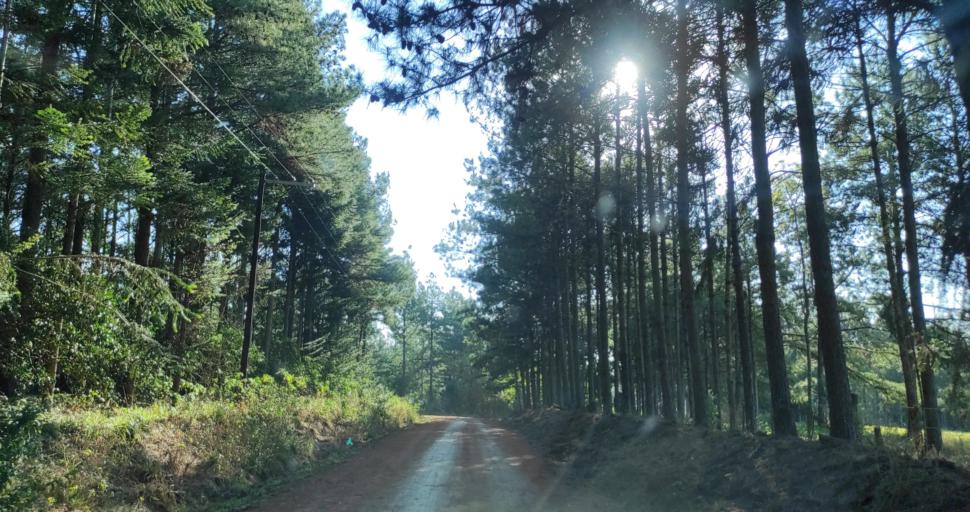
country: AR
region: Misiones
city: Capiovi
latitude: -26.8723
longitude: -55.1221
